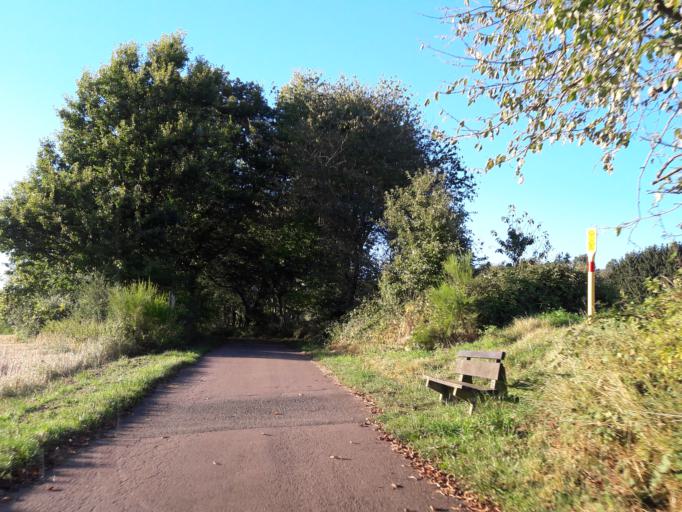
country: DE
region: Rheinland-Pfalz
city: Breitenbach
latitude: 49.4209
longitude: 7.2558
